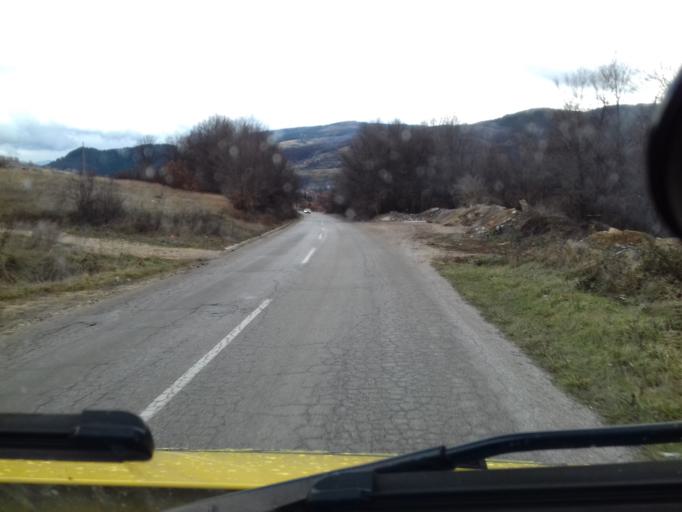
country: BA
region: Federation of Bosnia and Herzegovina
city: Turbe
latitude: 44.2524
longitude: 17.5559
